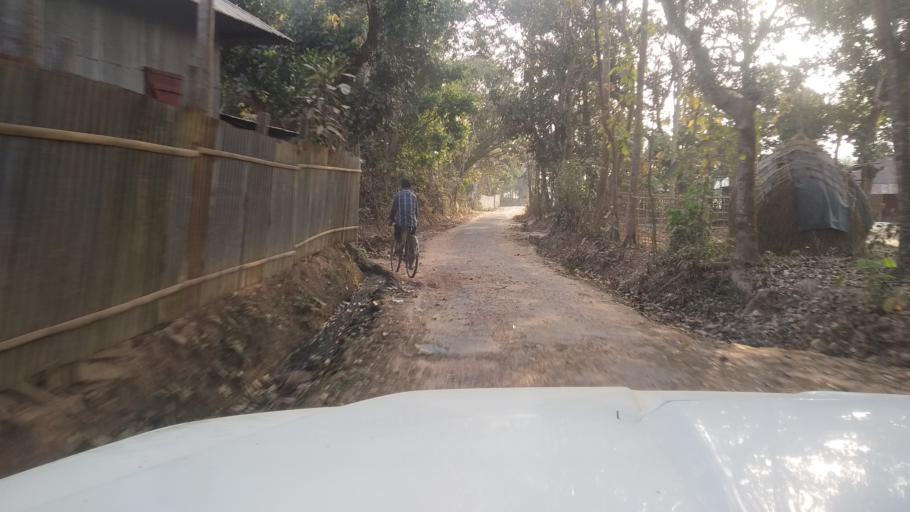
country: IN
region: Tripura
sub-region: West Tripura
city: Sonamura
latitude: 23.3251
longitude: 91.2970
